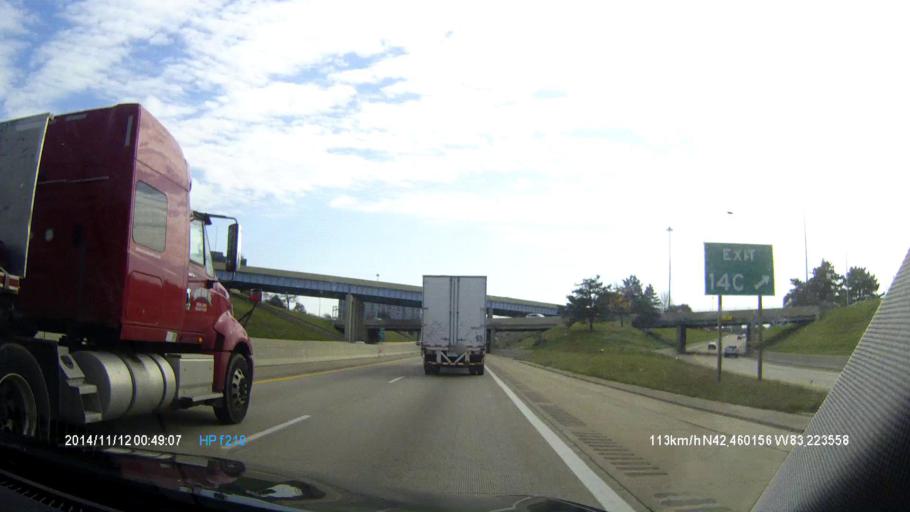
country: US
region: Michigan
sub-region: Oakland County
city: Southfield
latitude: 42.4600
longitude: -83.2233
